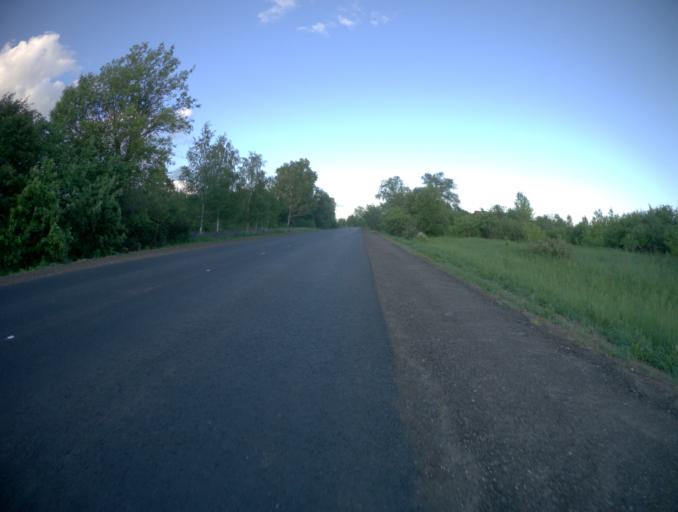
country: RU
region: Ivanovo
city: Gavrilov Posad
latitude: 56.5498
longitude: 40.1684
